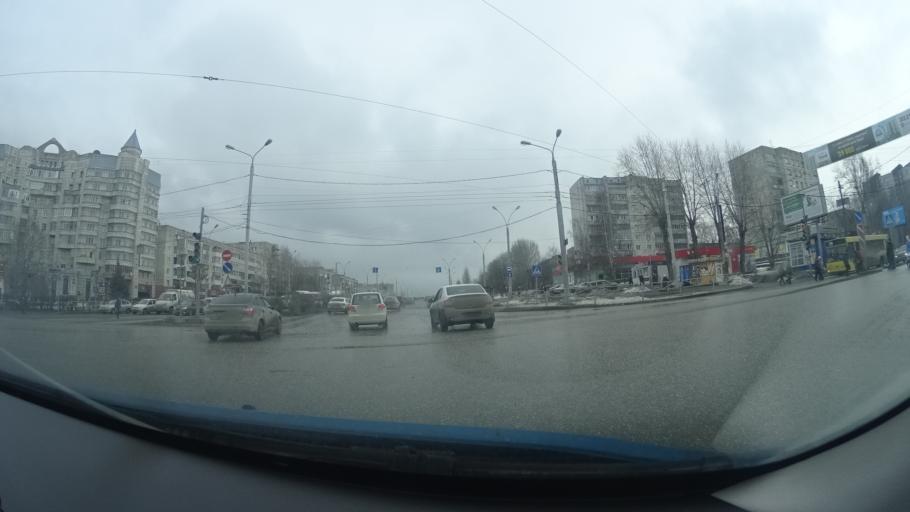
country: RU
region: Perm
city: Perm
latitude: 57.9861
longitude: 56.2167
